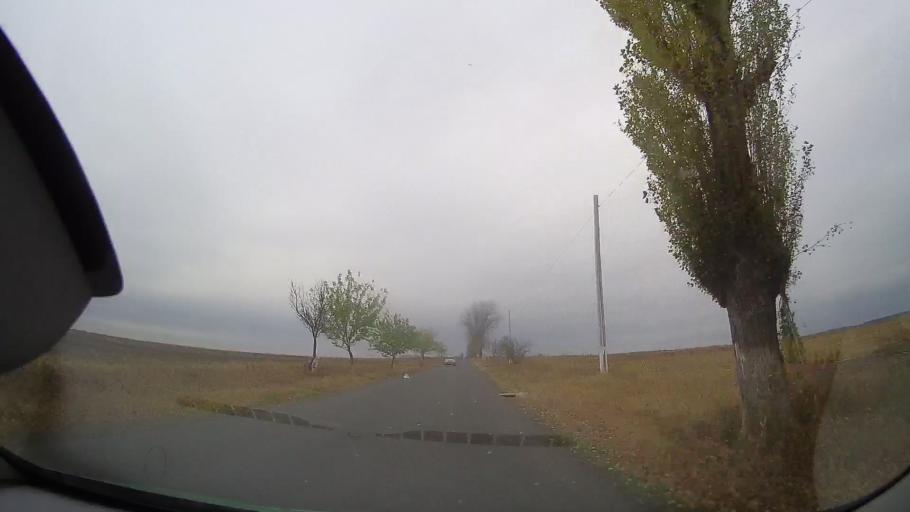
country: RO
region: Braila
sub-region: Comuna Budesti
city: Tataru
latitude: 44.8657
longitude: 27.4267
